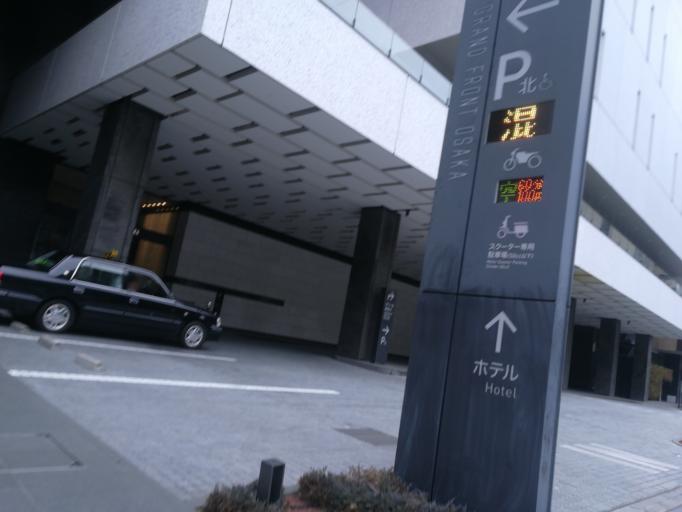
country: JP
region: Osaka
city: Osaka-shi
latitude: 34.7057
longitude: 135.4951
